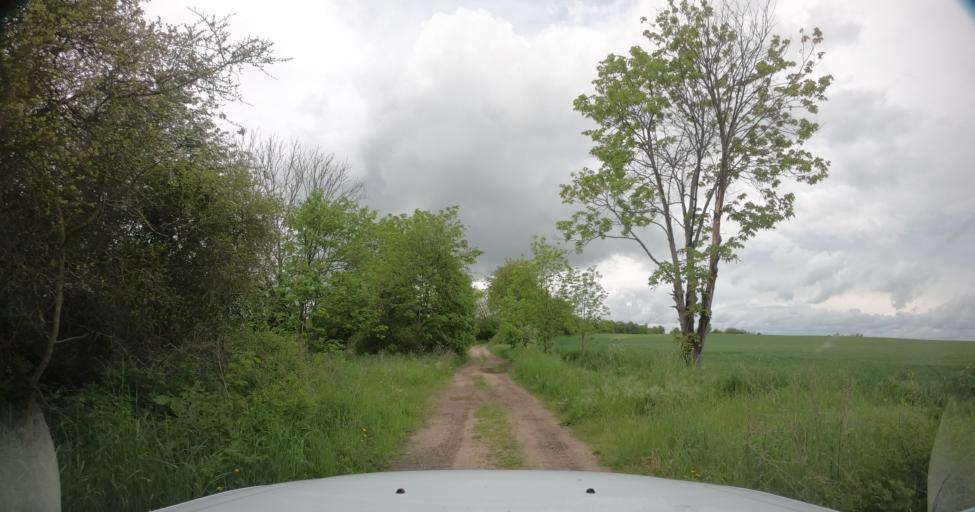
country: PL
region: West Pomeranian Voivodeship
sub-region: Powiat pyrzycki
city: Kozielice
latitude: 53.0821
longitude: 14.8289
